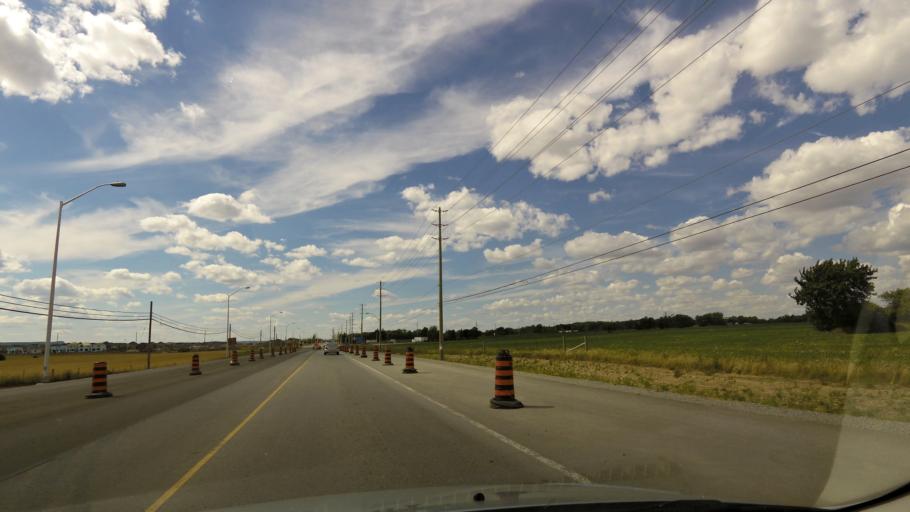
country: CA
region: Ontario
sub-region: Halton
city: Milton
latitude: 43.4841
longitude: -79.8310
